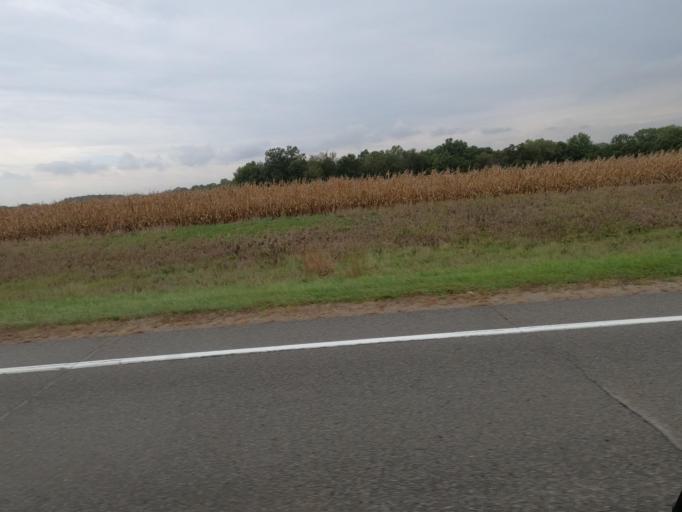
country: US
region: Iowa
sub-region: Van Buren County
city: Keosauqua
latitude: 40.8121
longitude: -91.9137
